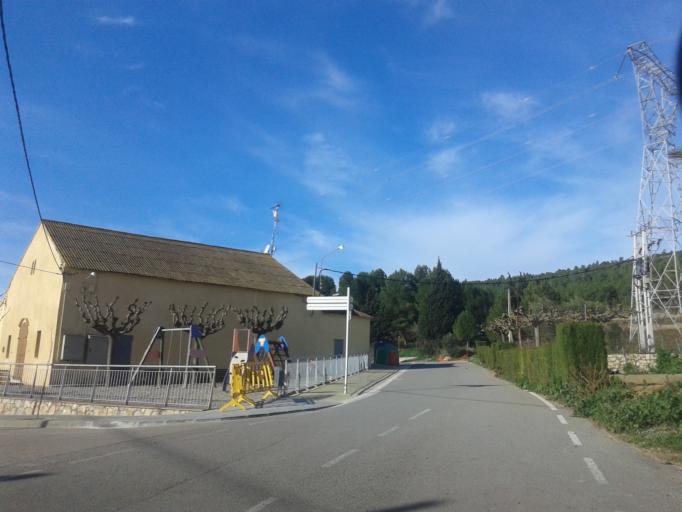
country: ES
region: Catalonia
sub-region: Provincia de Barcelona
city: Avinyonet del Penedes
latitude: 41.3337
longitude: 1.7653
